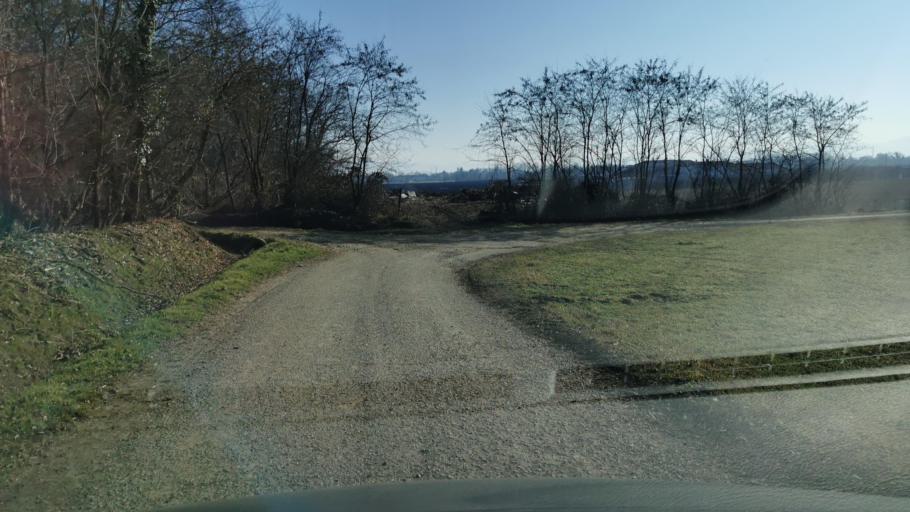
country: IT
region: Piedmont
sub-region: Provincia di Torino
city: Leini
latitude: 45.2135
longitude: 7.6923
